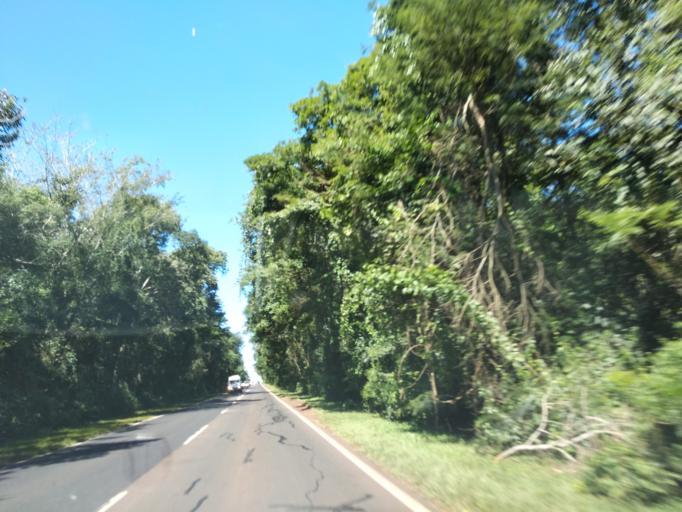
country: AR
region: Misiones
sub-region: Departamento de Iguazu
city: Puerto Iguazu
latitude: -25.6499
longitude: -54.5229
